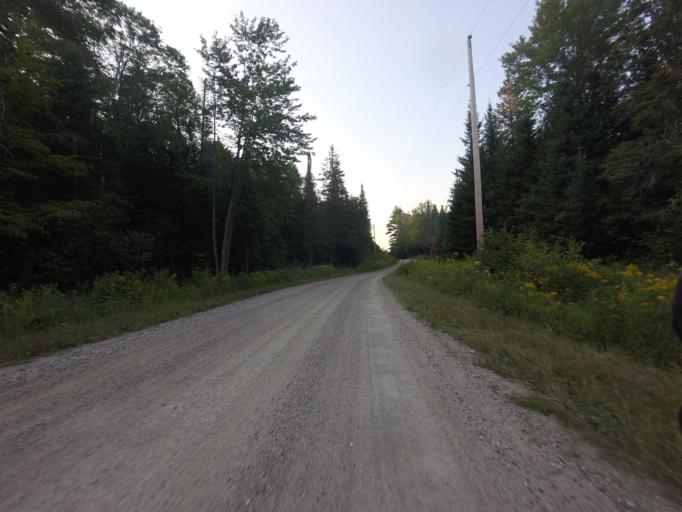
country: CA
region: Ontario
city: Renfrew
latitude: 45.0532
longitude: -76.7497
